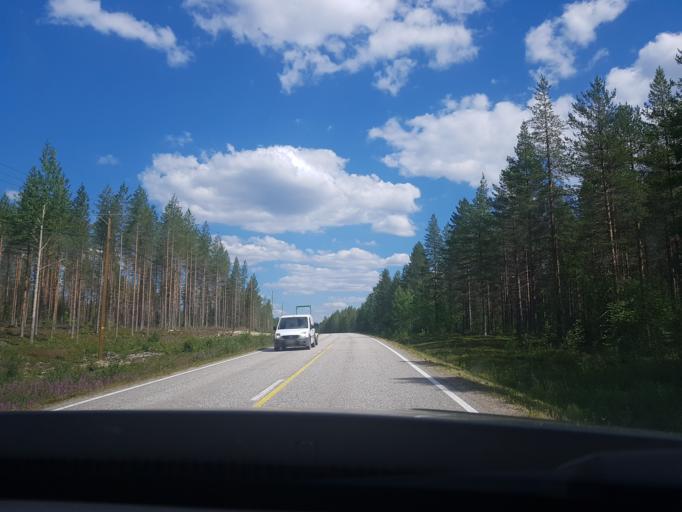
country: FI
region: Kainuu
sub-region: Kehys-Kainuu
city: Kuhmo
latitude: 64.2048
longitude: 29.7172
